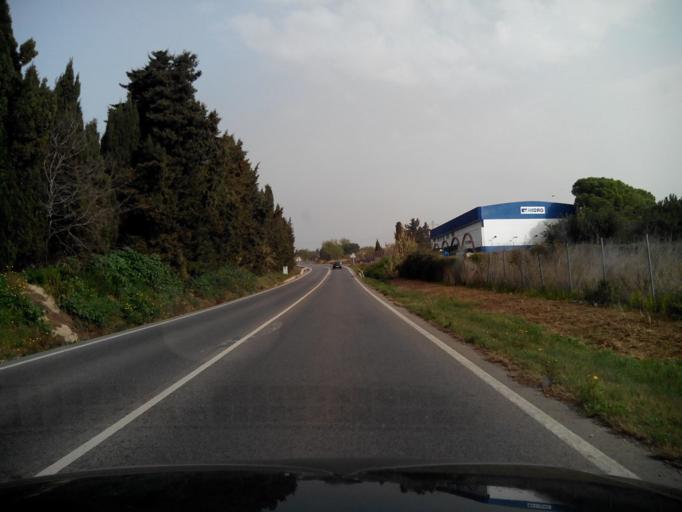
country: ES
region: Catalonia
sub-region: Provincia de Tarragona
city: Reus
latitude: 41.1231
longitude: 1.0959
